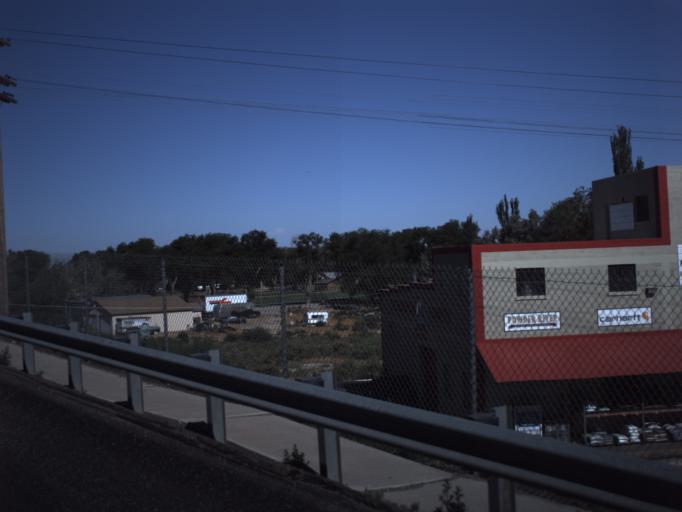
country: US
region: Utah
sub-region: Millard County
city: Delta
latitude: 39.3525
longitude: -112.5858
